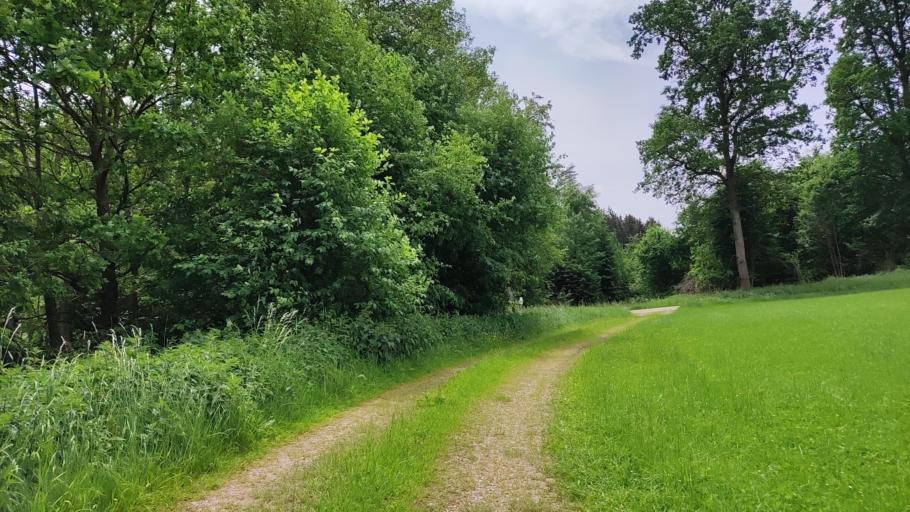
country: DE
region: Bavaria
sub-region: Swabia
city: Landensberg
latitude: 48.4288
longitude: 10.5091
